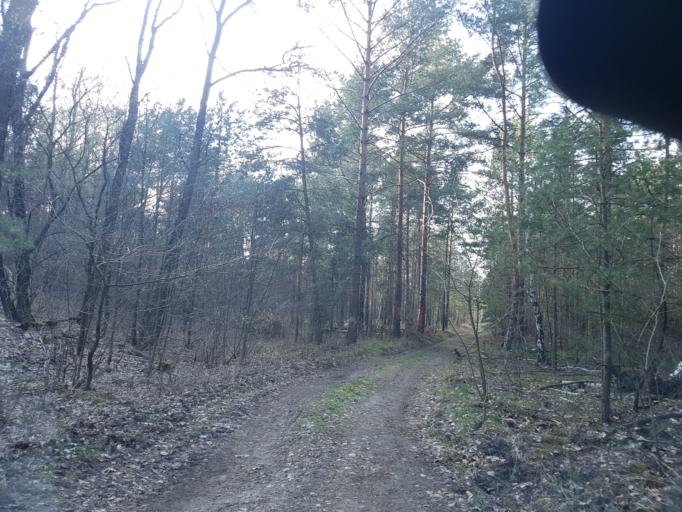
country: DE
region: Brandenburg
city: Trobitz
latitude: 51.6045
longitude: 13.4603
